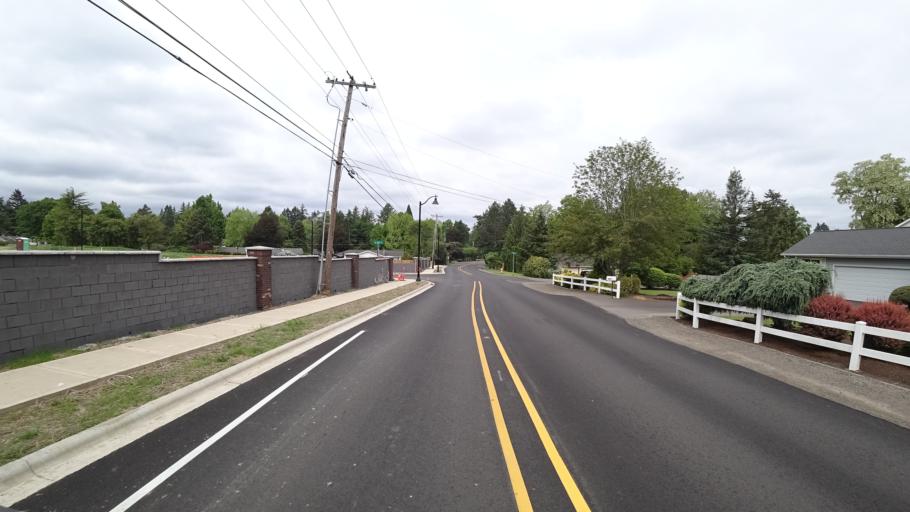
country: US
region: Oregon
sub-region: Washington County
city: Raleigh Hills
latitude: 45.4795
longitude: -122.7656
